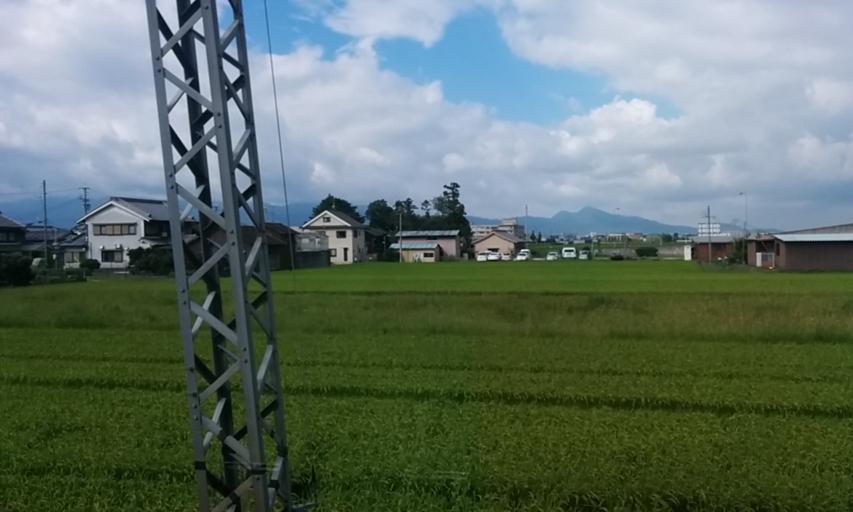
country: JP
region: Nara
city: Kashihara-shi
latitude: 34.5311
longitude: 135.7943
